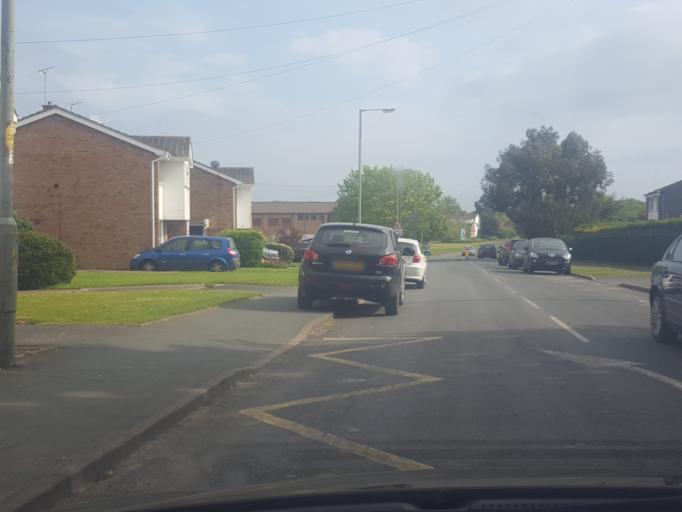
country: GB
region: England
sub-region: Essex
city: Frinton-on-Sea
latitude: 51.8461
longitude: 1.2478
